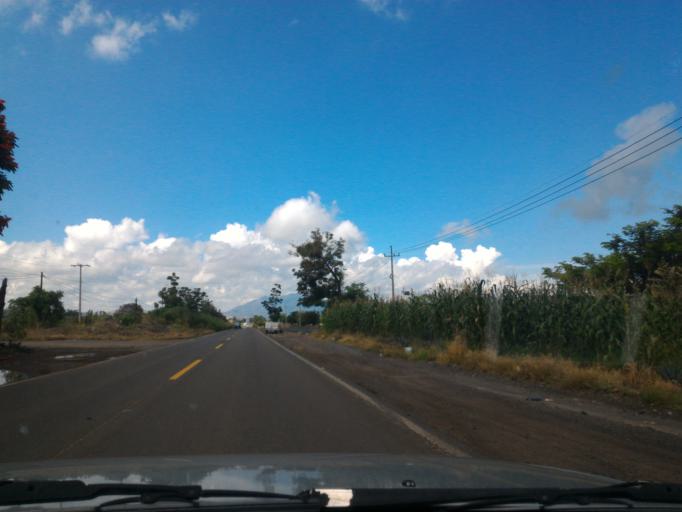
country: MX
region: Jalisco
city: Tequila
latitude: 20.8684
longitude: -103.7885
